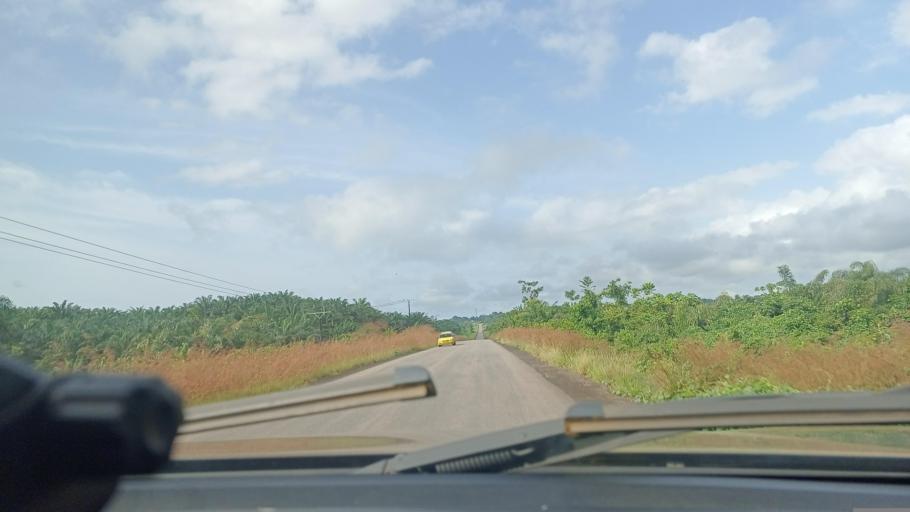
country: LR
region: Bomi
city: Tubmanburg
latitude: 6.7249
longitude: -11.0481
